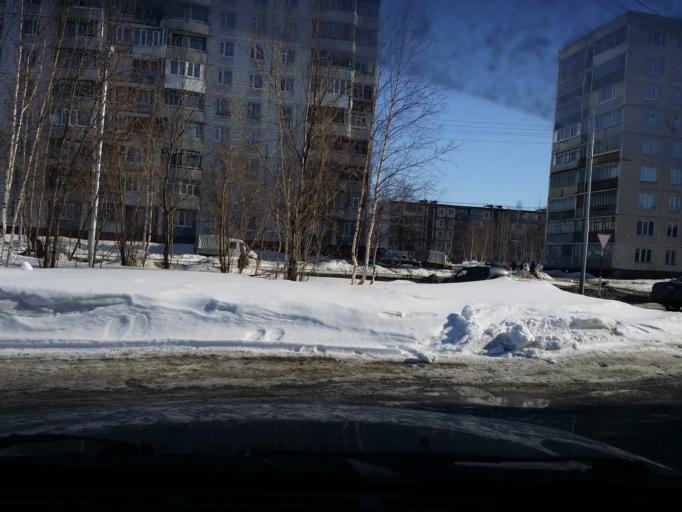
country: RU
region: Khanty-Mansiyskiy Avtonomnyy Okrug
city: Nizhnevartovsk
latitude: 60.9378
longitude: 76.6074
